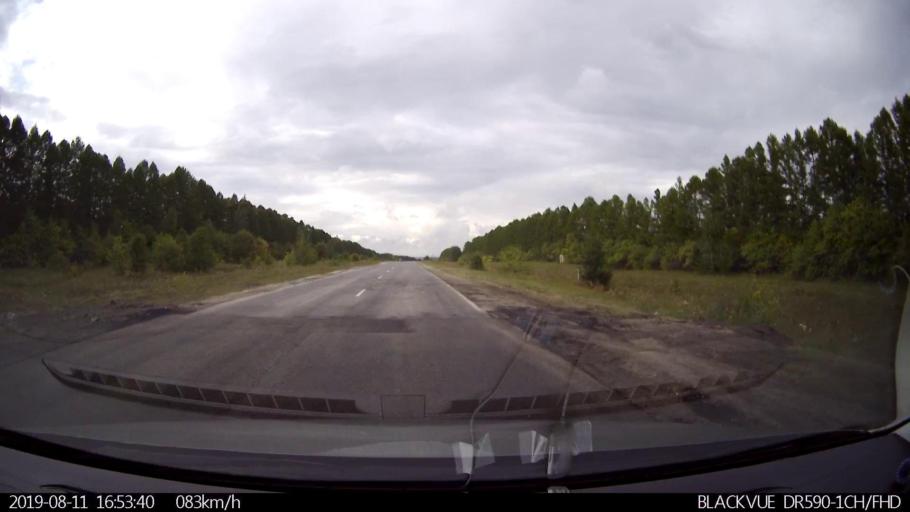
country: RU
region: Ulyanovsk
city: Mayna
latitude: 54.2649
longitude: 47.6695
